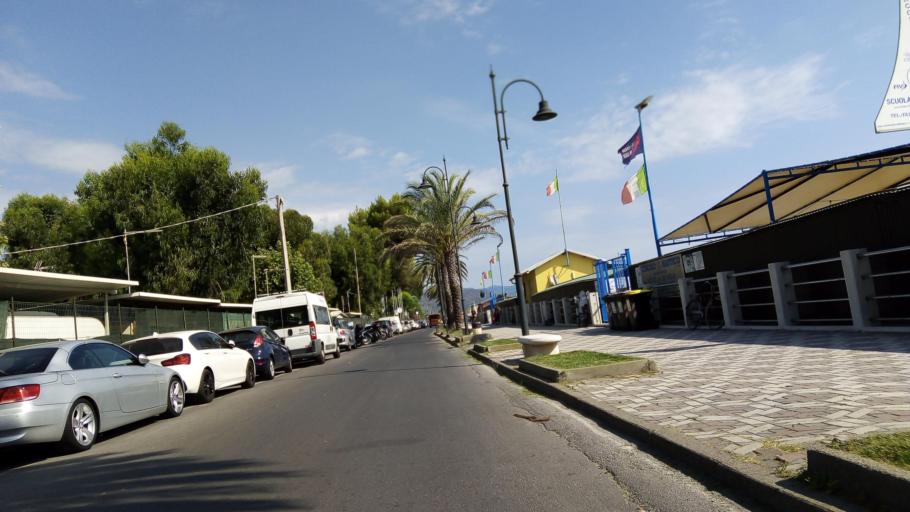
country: IT
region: Liguria
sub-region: Provincia di Savona
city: Albenga
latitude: 44.0505
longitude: 8.2257
